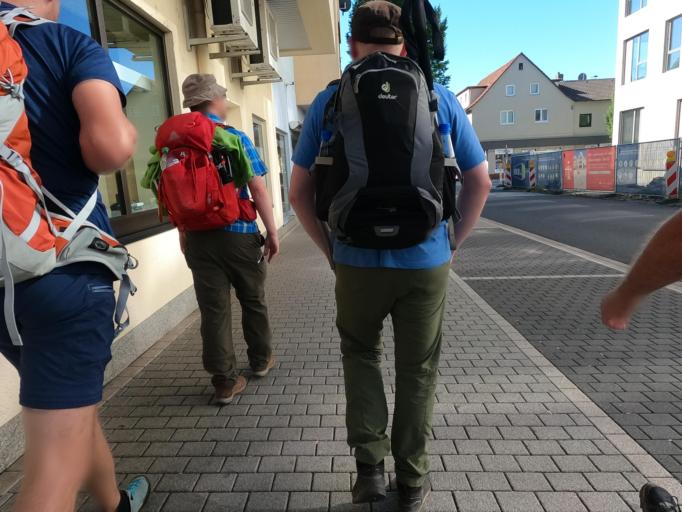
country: DE
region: Hesse
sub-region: Regierungsbezirk Darmstadt
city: Schluchtern
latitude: 50.3506
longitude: 9.5258
